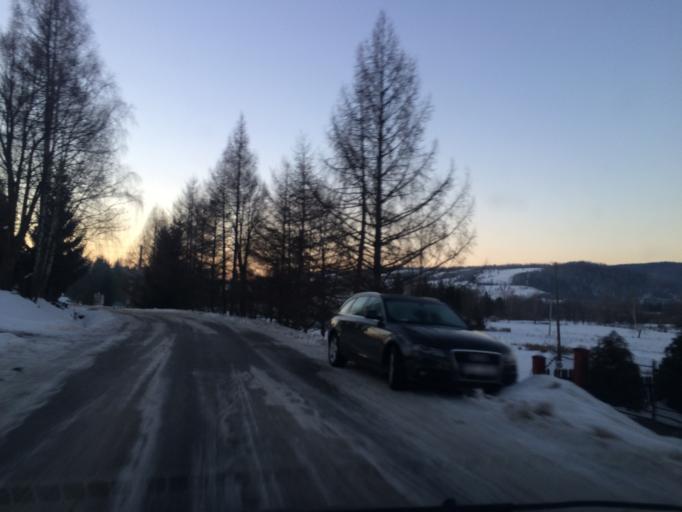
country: PL
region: Subcarpathian Voivodeship
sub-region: Powiat bieszczadzki
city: Ustrzyki Dolne
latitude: 49.4121
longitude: 22.5821
